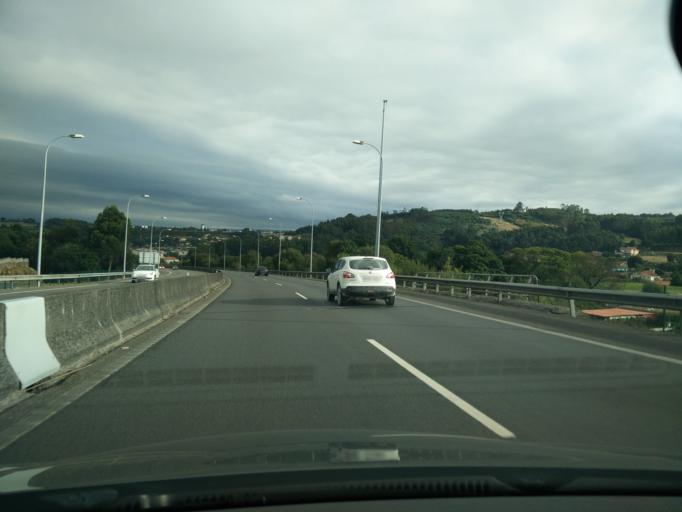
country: ES
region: Galicia
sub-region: Provincia da Coruna
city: Culleredo
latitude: 43.3182
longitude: -8.3919
